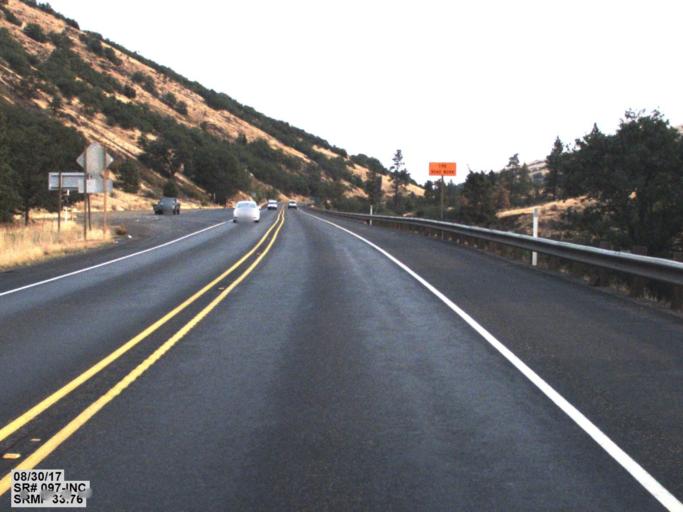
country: US
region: Washington
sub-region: Klickitat County
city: Goldendale
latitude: 46.0447
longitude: -120.5719
